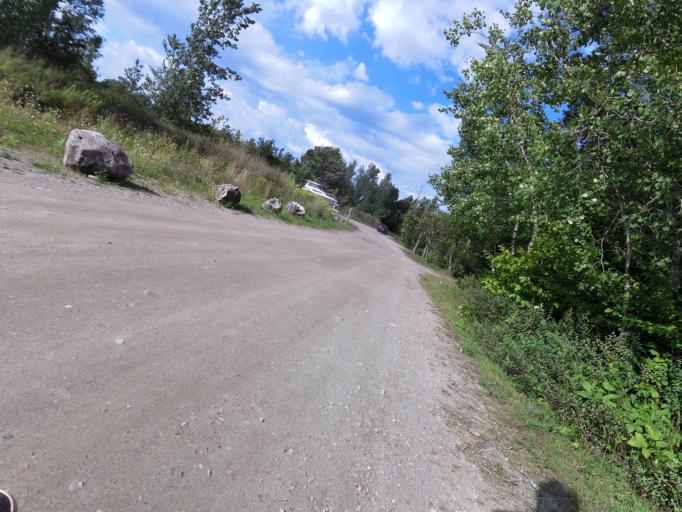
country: CA
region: Ontario
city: Tobermory
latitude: 45.2320
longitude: -81.6445
